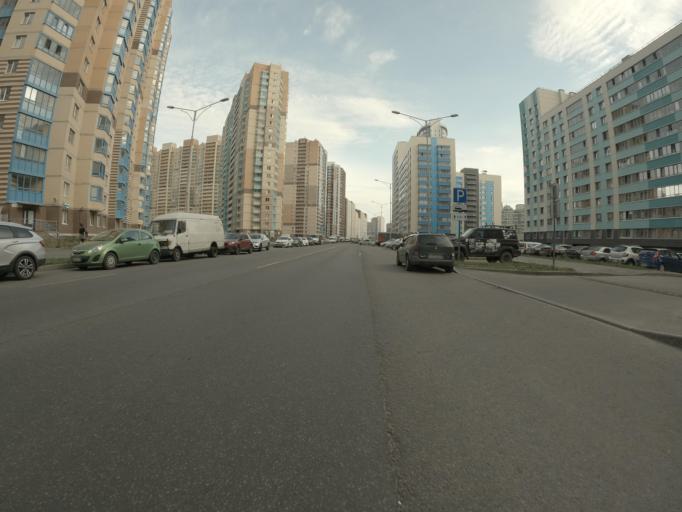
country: RU
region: Leningrad
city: Rybatskoye
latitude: 59.9052
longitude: 30.5127
